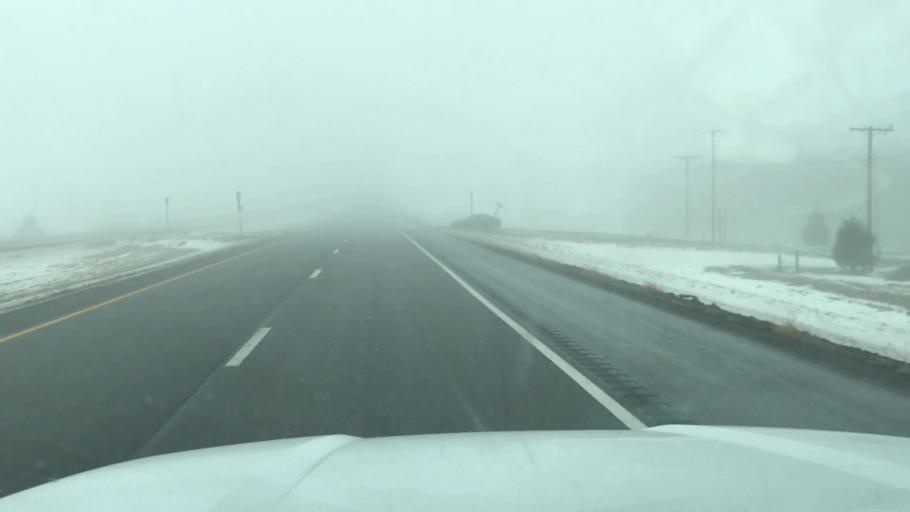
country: US
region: Missouri
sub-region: Clinton County
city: Cameron
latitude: 39.7541
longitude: -94.2619
